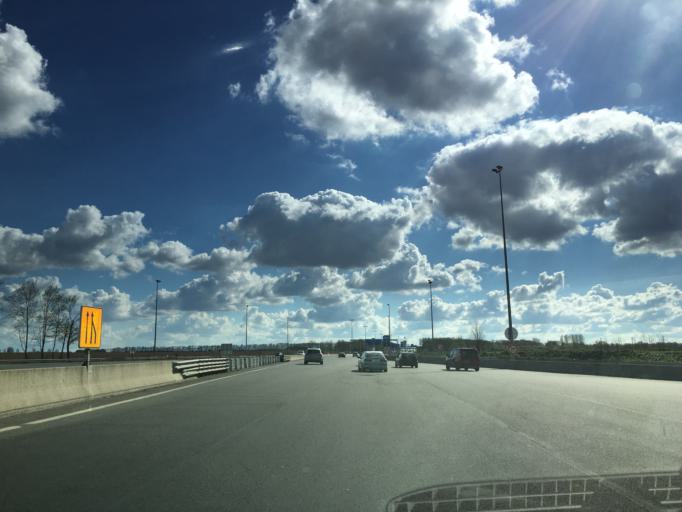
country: FR
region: Nord-Pas-de-Calais
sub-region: Departement du Pas-de-Calais
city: Roeux
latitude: 50.3243
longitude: 2.9103
